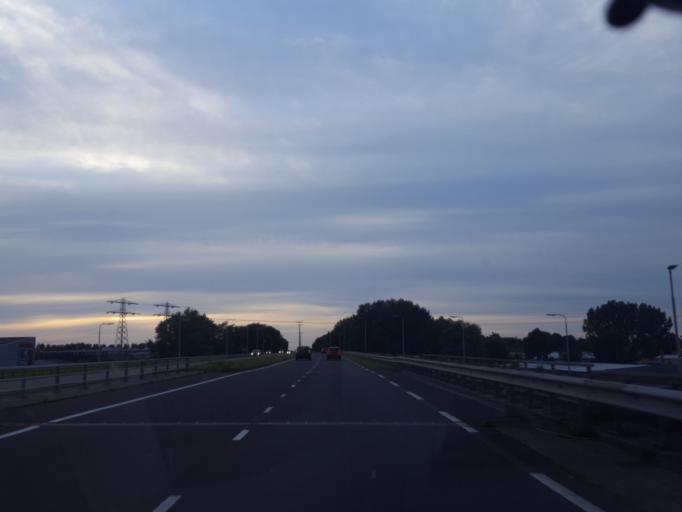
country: NL
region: Friesland
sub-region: Gemeente Leeuwarden
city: Camminghaburen
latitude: 53.1985
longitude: 5.8387
